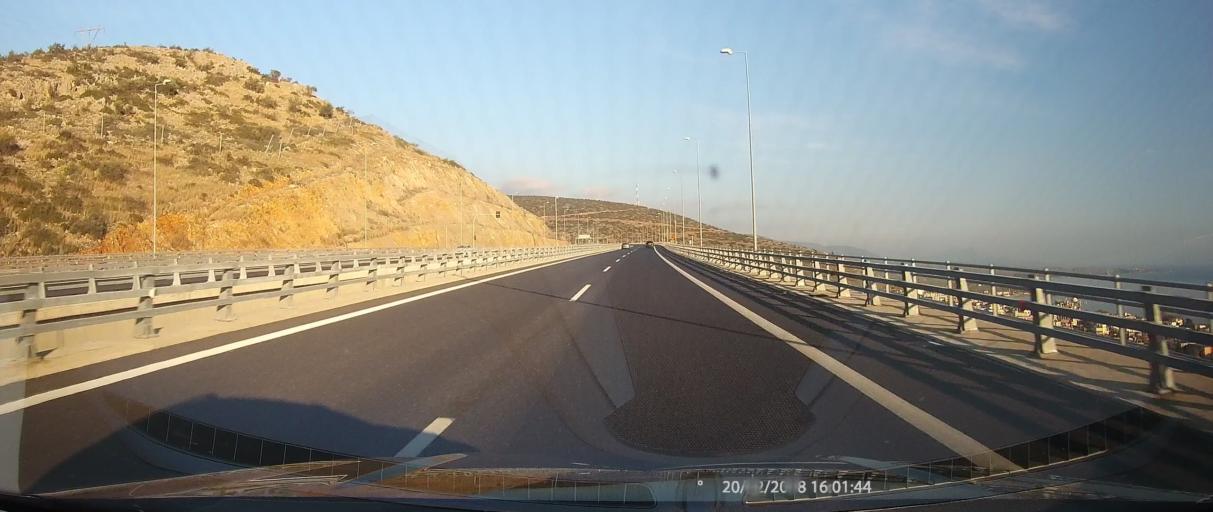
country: GR
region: Central Greece
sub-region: Nomos Fthiotidos
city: Stylida
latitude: 38.9165
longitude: 22.5971
